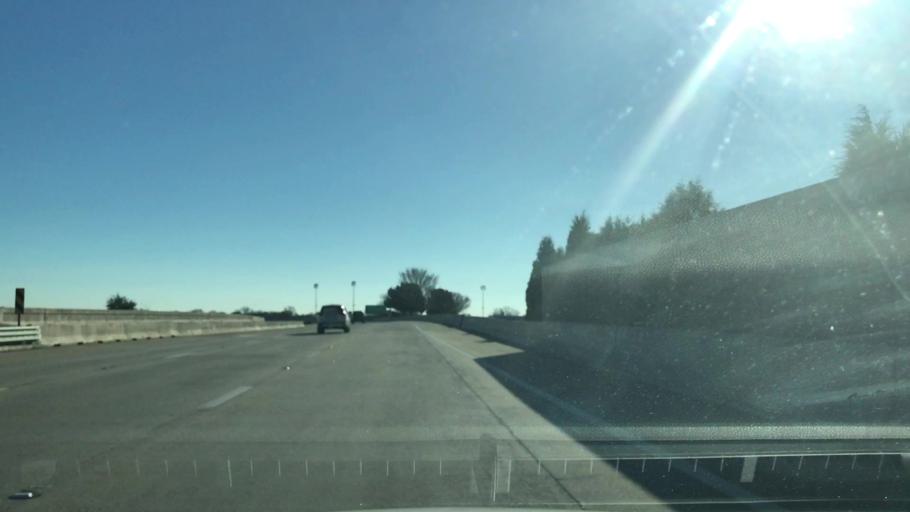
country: US
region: Texas
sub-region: Dallas County
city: Coppell
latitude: 32.9830
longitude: -96.9961
